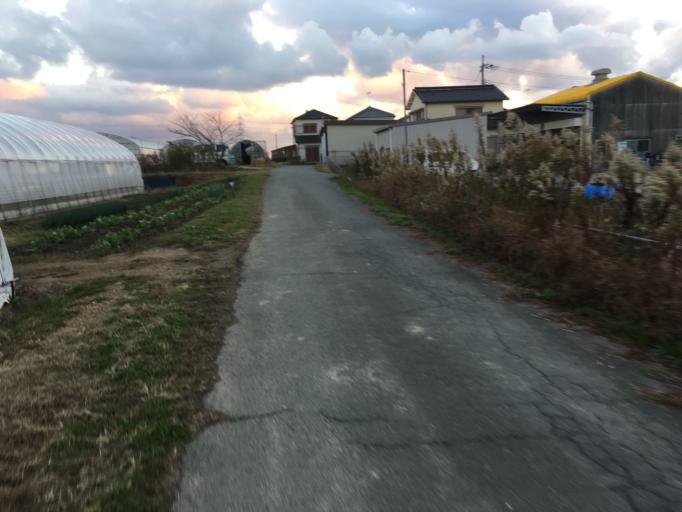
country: JP
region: Hyogo
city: Miki
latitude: 34.7346
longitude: 134.9498
